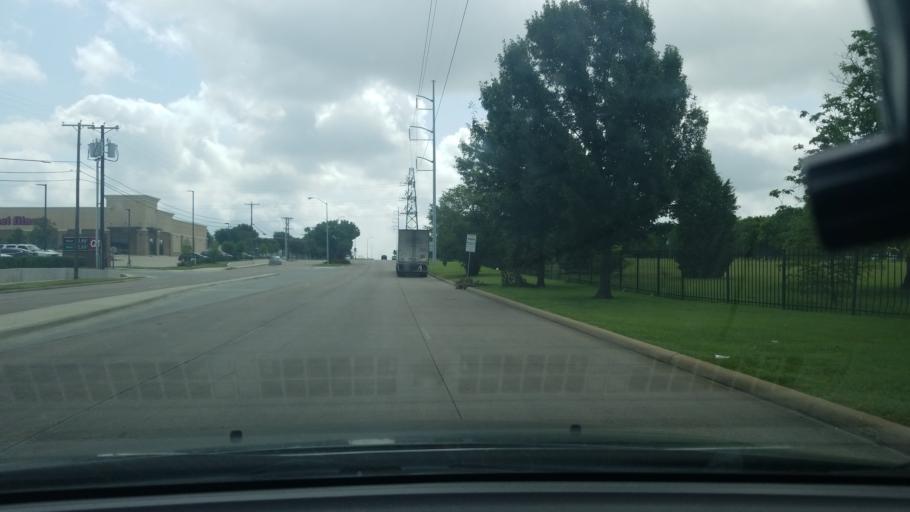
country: US
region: Texas
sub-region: Dallas County
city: Balch Springs
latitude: 32.7924
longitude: -96.6847
